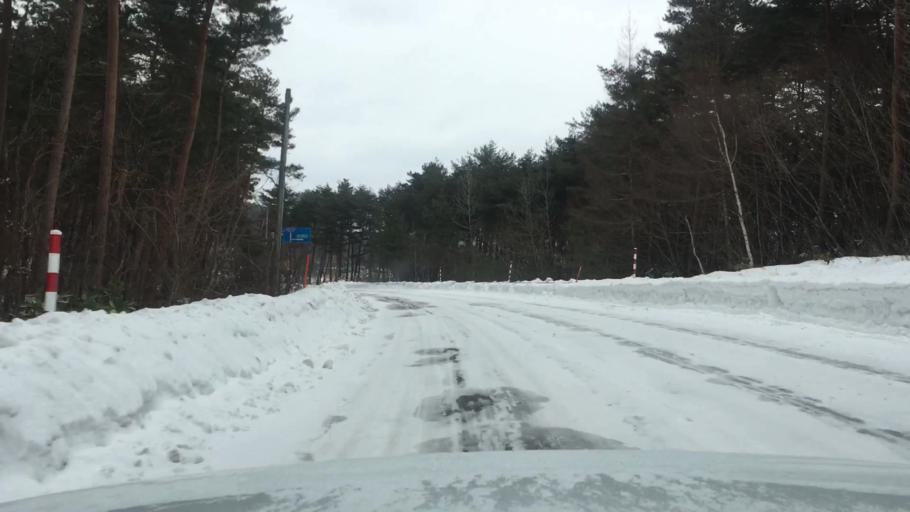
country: JP
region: Iwate
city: Shizukuishi
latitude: 39.9470
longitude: 140.9983
